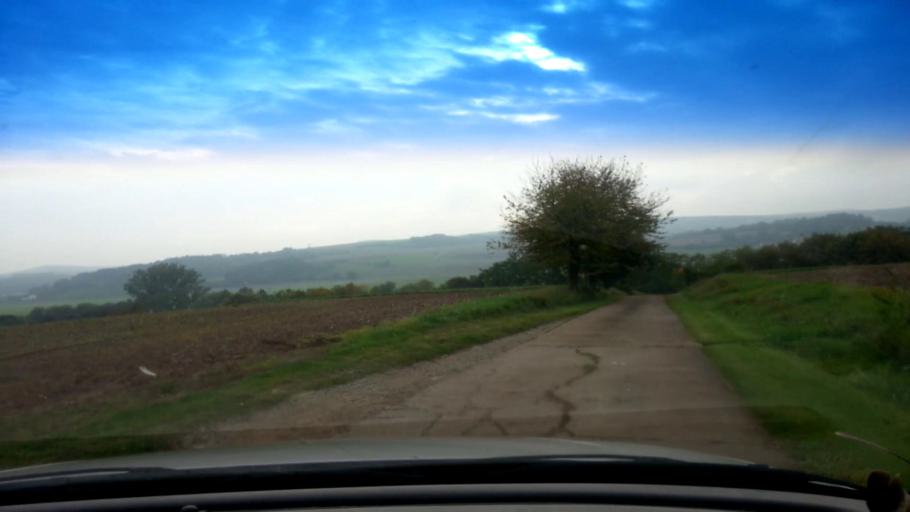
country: DE
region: Bavaria
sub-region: Upper Franconia
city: Rattelsdorf
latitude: 50.0609
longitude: 10.8787
